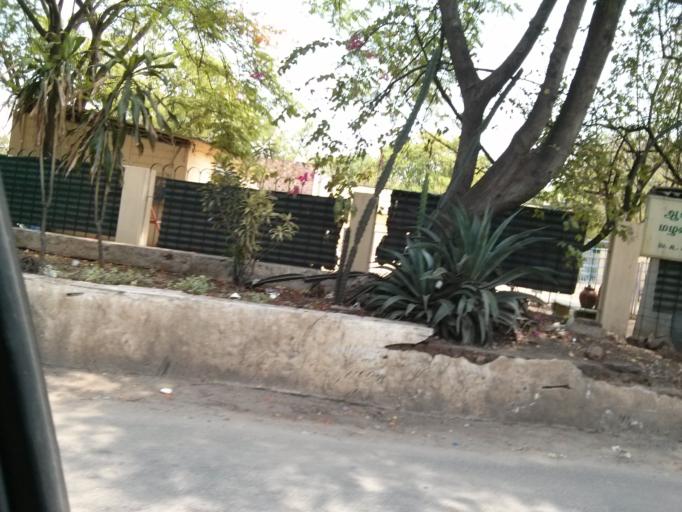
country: IN
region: Tamil Nadu
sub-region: Coimbatore
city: Coimbatore
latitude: 11.0081
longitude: 76.9709
